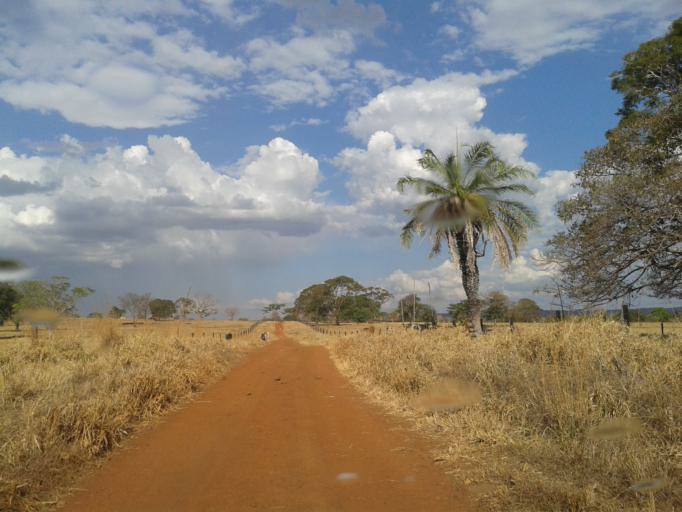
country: BR
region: Minas Gerais
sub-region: Santa Vitoria
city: Santa Vitoria
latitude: -19.1691
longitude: -49.9977
